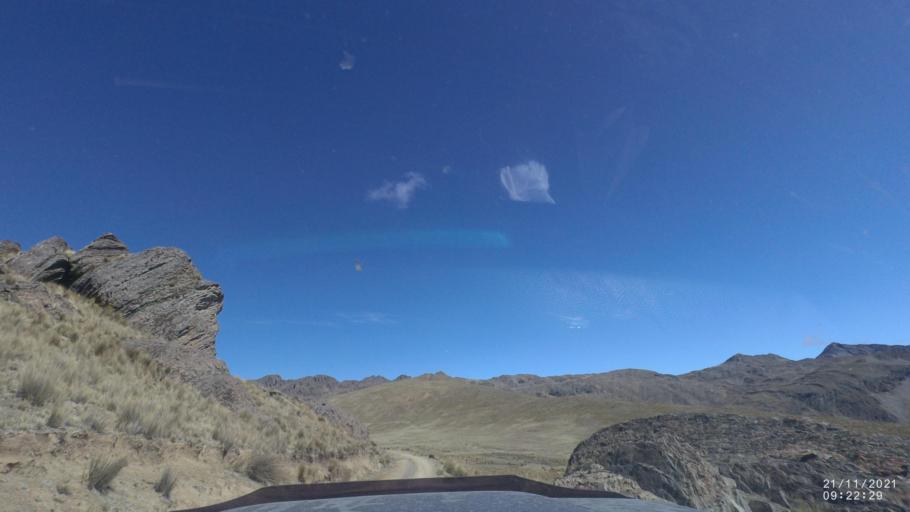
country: BO
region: Cochabamba
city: Cochabamba
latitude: -17.1006
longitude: -66.2486
